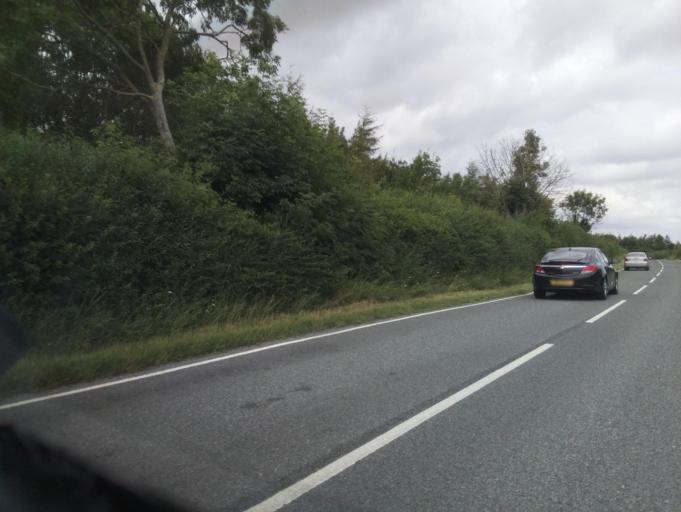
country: GB
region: England
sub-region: District of Rutland
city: Ryhall
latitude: 52.6829
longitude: -0.5019
